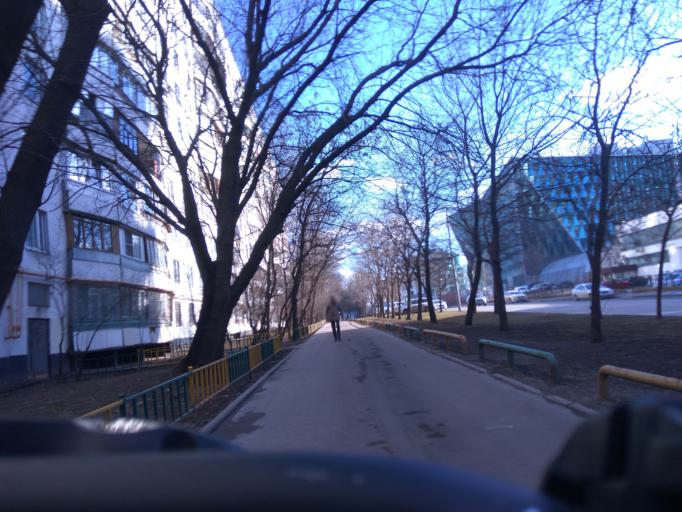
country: RU
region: Moscow
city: Ostankinskiy
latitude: 55.8195
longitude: 37.6209
